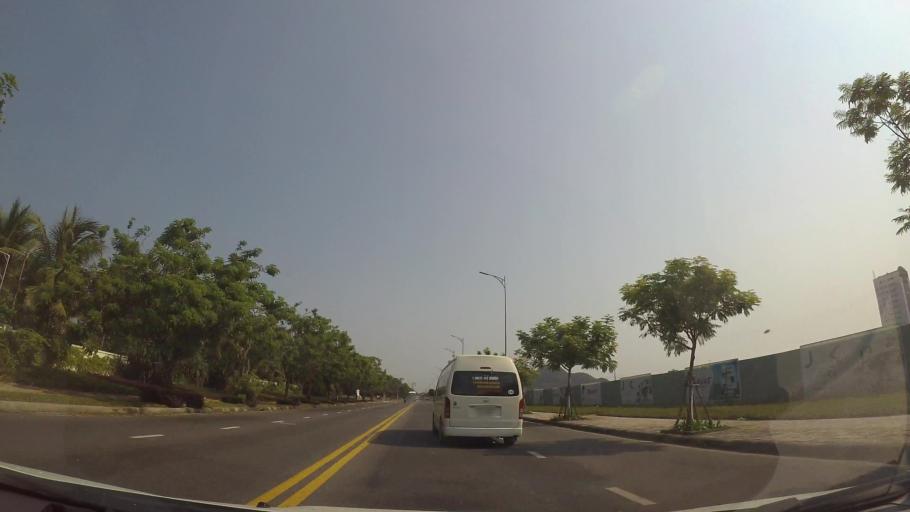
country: VN
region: Da Nang
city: Ngu Hanh Son
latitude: 16.0162
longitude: 108.2605
